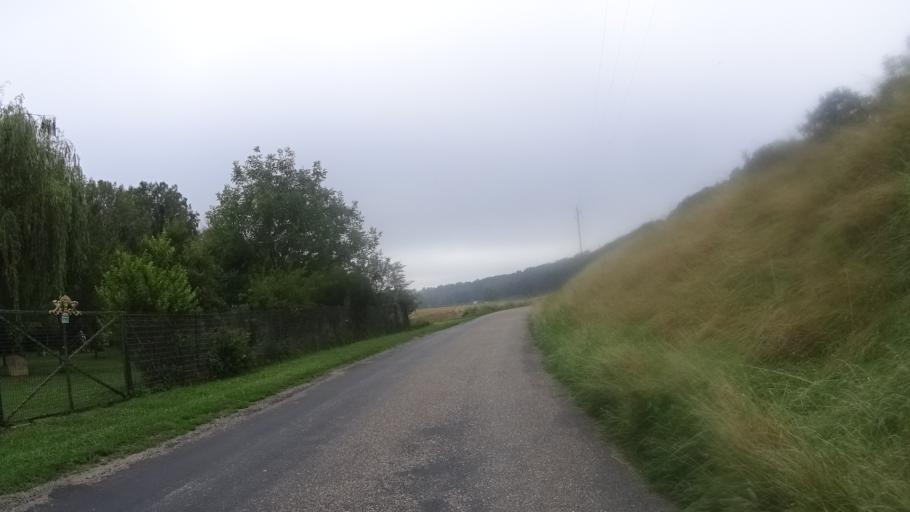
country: FR
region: Lorraine
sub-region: Departement de la Meuse
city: Revigny-sur-Ornain
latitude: 48.8149
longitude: 5.0442
